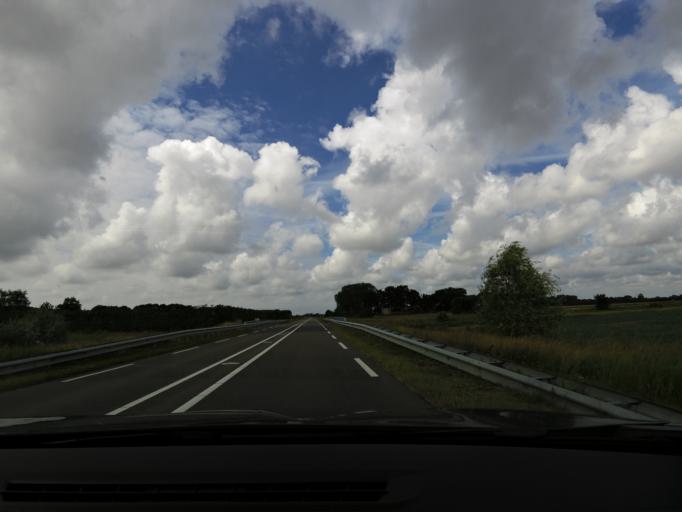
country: NL
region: Zeeland
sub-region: Gemeente Vlissingen
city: Vlissingen
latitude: 51.4714
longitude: 3.5667
